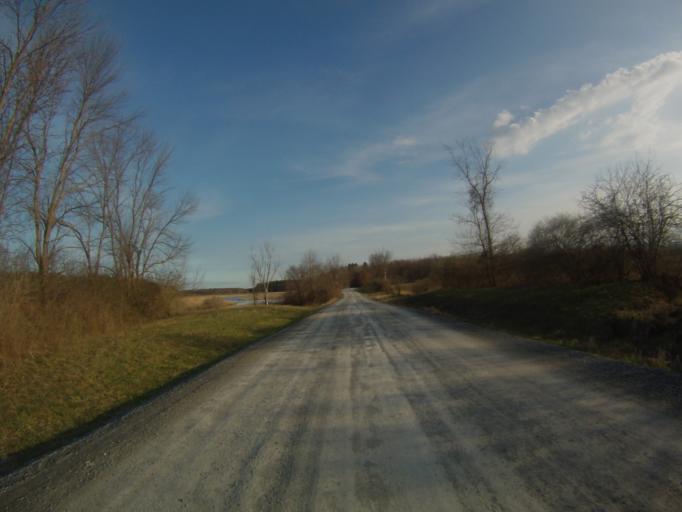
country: US
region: New York
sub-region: Essex County
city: Port Henry
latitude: 44.0802
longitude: -73.3512
